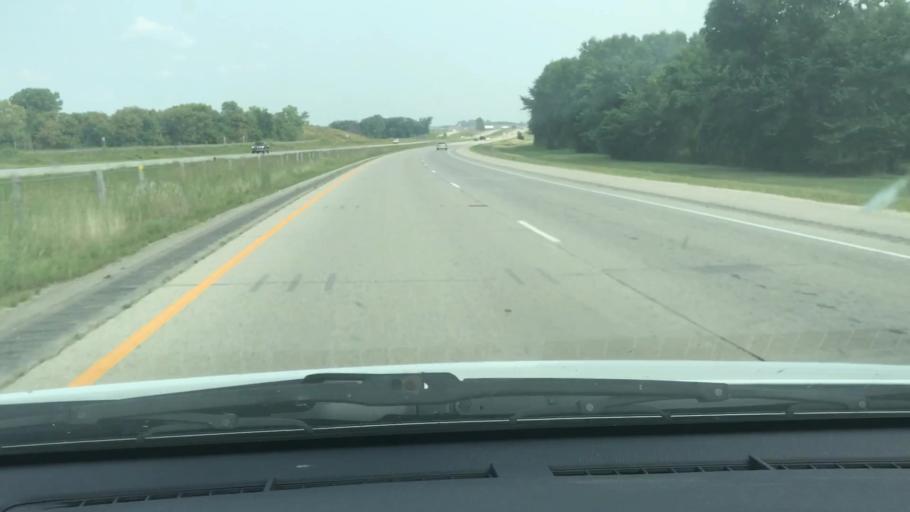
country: US
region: Minnesota
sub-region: Goodhue County
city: Pine Island
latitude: 44.2008
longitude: -92.6150
